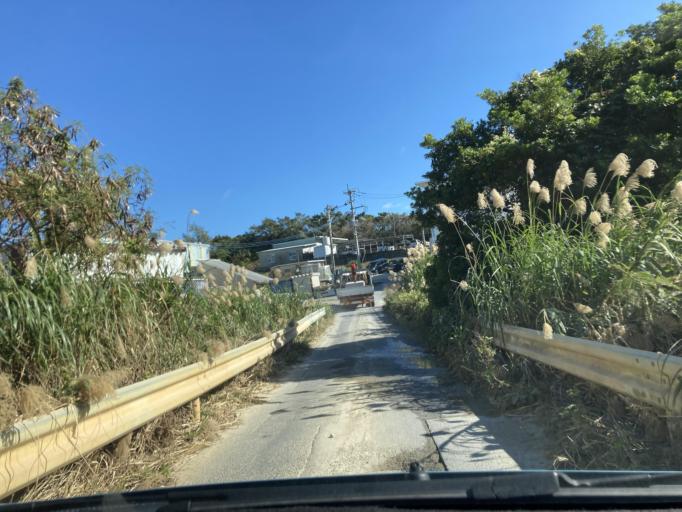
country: JP
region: Okinawa
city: Gushikawa
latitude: 26.3674
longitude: 127.8277
